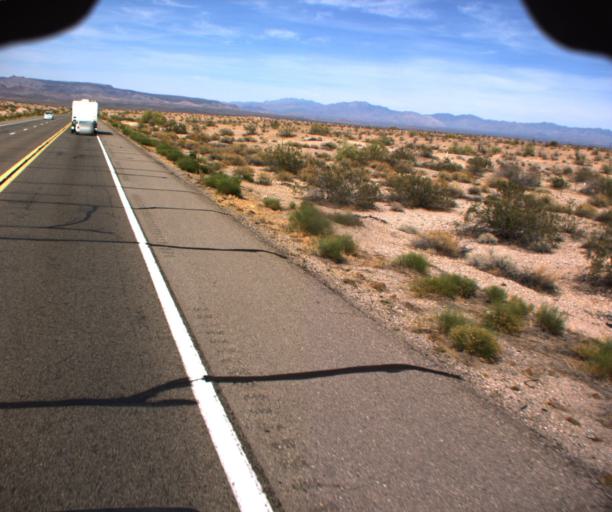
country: US
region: Arizona
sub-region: Mohave County
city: Desert Hills
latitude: 34.6774
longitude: -114.3074
